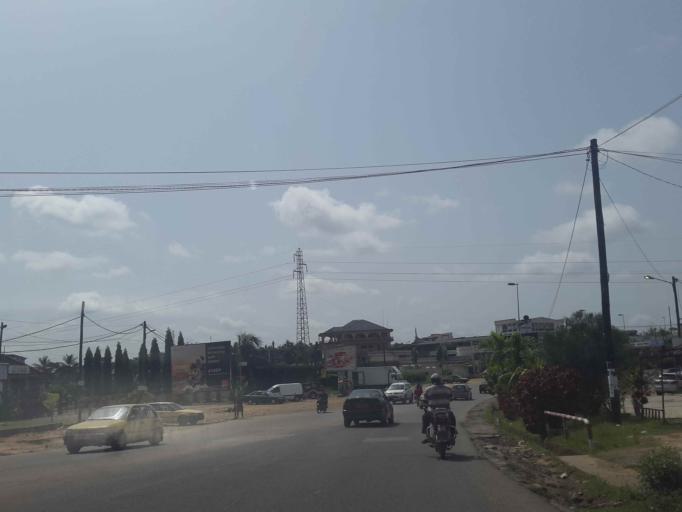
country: CM
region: Littoral
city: Douala
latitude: 4.0843
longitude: 9.7437
